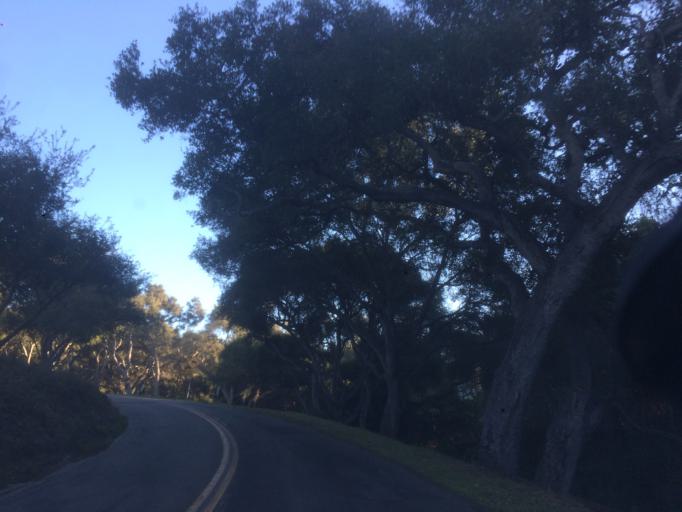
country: US
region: California
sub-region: Santa Barbara County
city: Goleta
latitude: 34.4154
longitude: -119.7724
